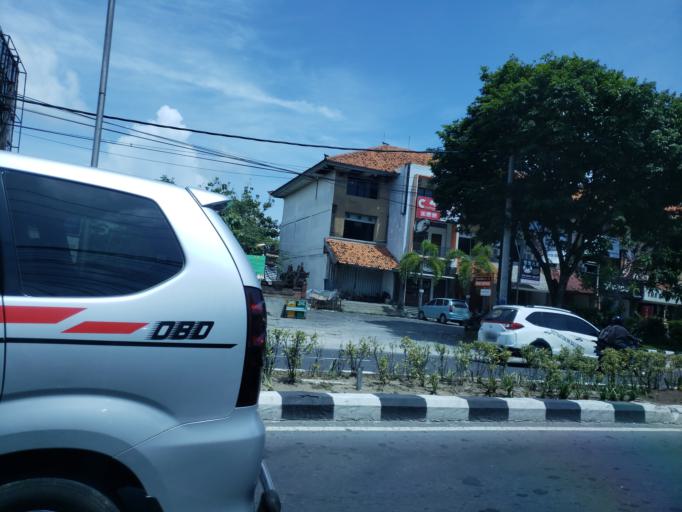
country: ID
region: Bali
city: Jabajero
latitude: -8.7363
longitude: 115.1795
